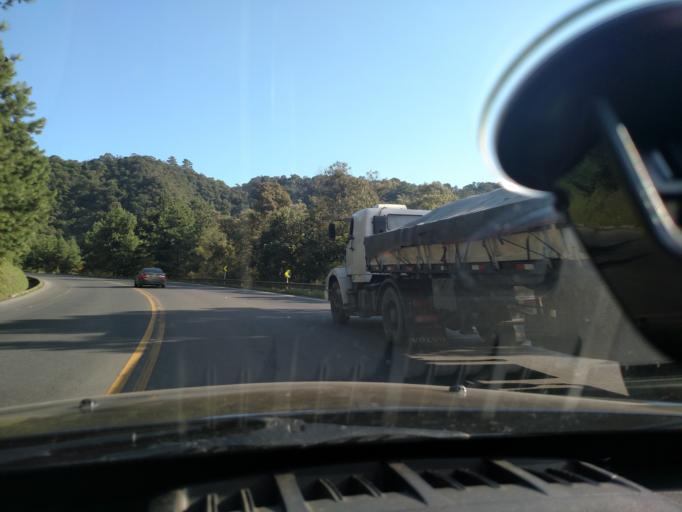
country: BR
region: Santa Catarina
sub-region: Otacilio Costa
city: Otacilio Costa
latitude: -27.2989
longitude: -50.0760
